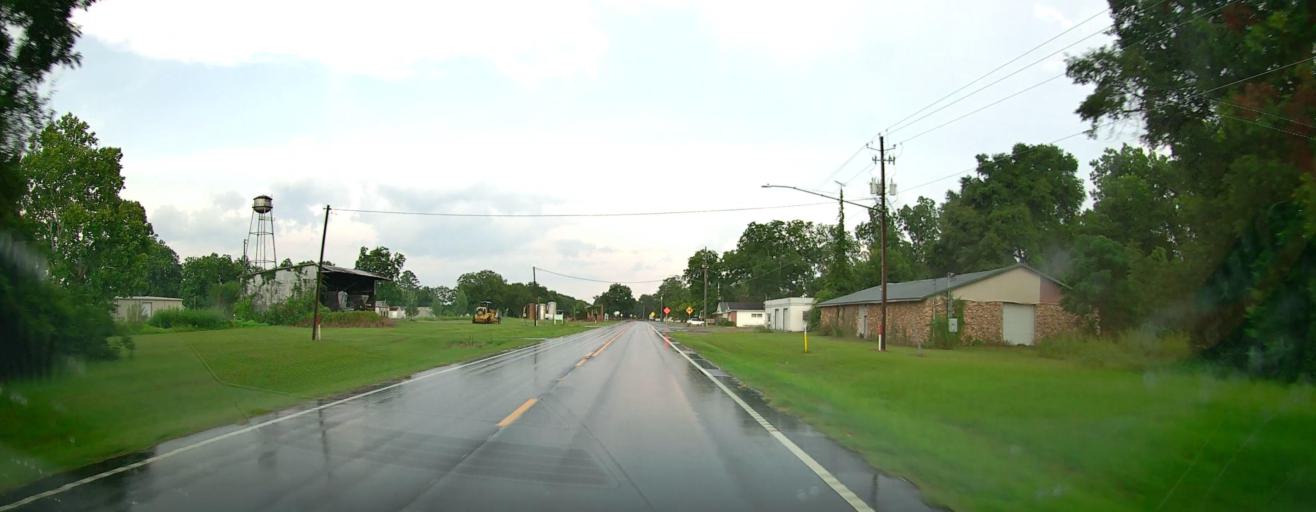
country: US
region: Georgia
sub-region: Dodge County
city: Chester
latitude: 32.5605
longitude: -83.1561
